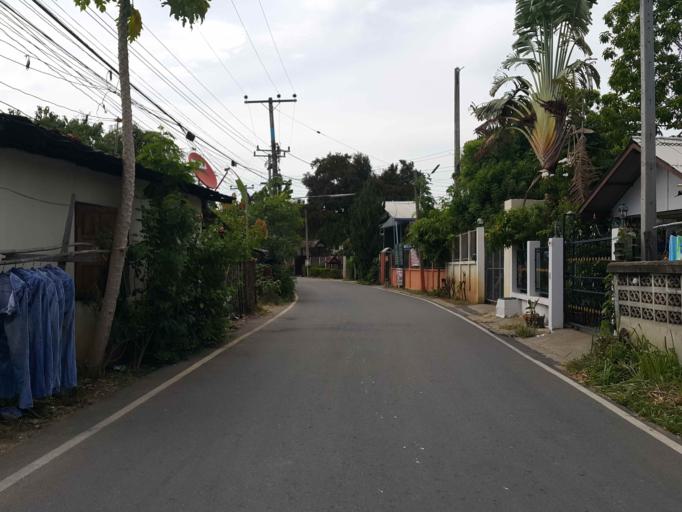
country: TH
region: Chiang Mai
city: Saraphi
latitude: 18.7470
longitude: 99.0148
